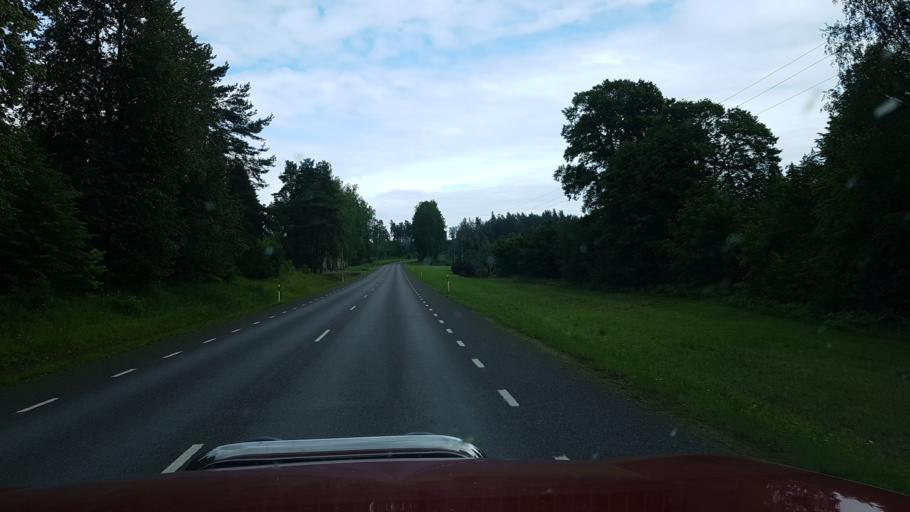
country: EE
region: Polvamaa
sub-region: Raepina vald
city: Rapina
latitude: 58.0959
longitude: 27.3534
